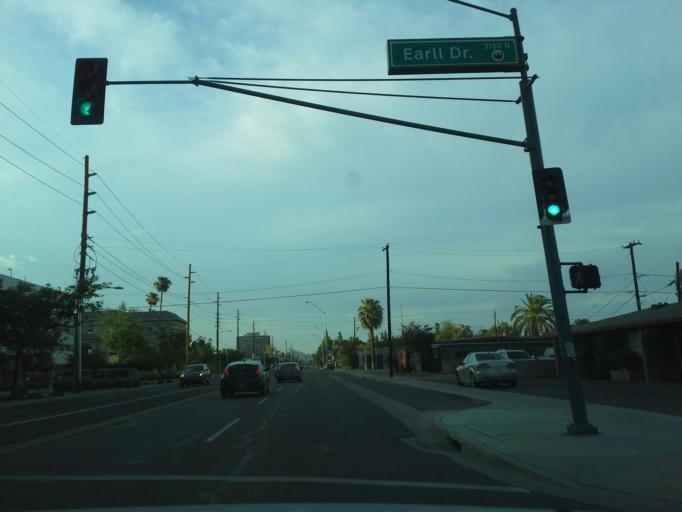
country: US
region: Arizona
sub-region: Maricopa County
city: Phoenix
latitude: 33.4838
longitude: -112.0694
